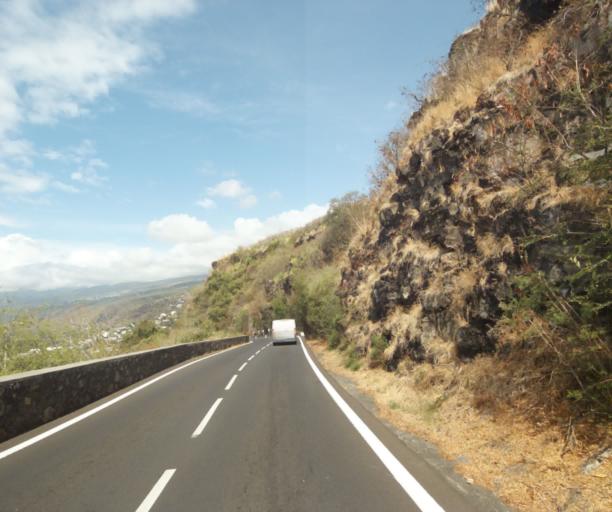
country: RE
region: Reunion
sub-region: Reunion
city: Saint-Paul
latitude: -21.0162
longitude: 55.2679
